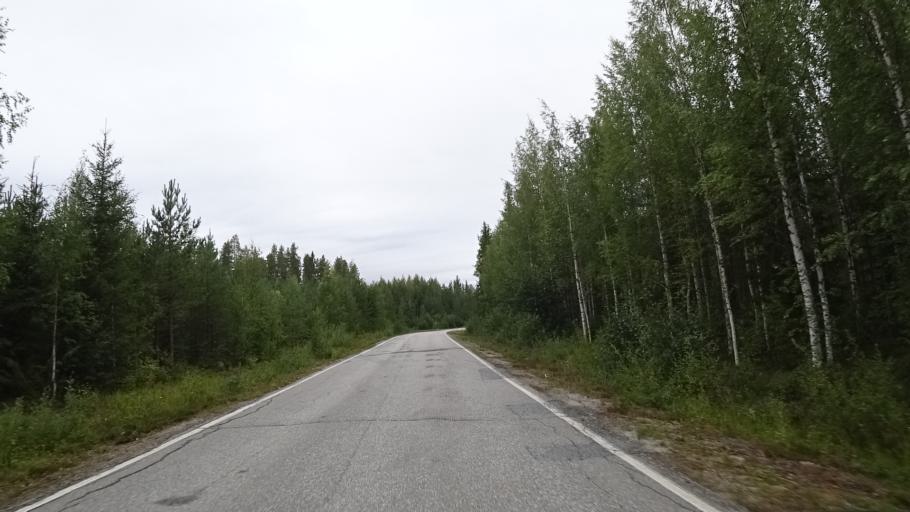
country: FI
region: North Karelia
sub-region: Pielisen Karjala
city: Lieksa
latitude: 63.3563
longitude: 30.2618
